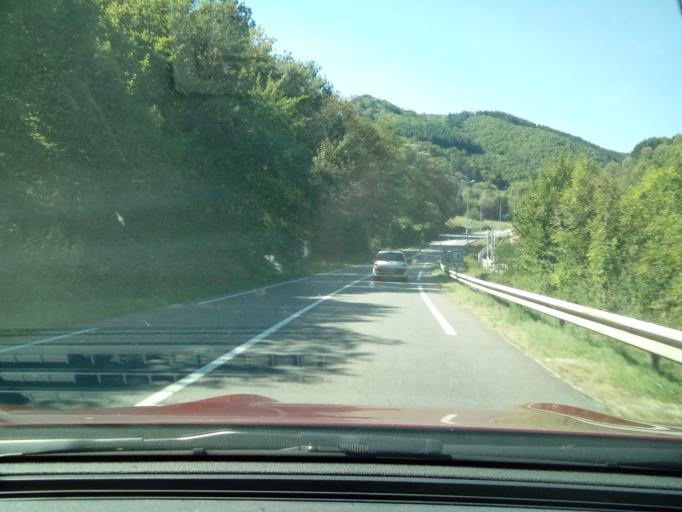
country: FR
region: Rhone-Alpes
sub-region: Departement du Rhone
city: Tarare
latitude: 45.9235
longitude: 4.4522
